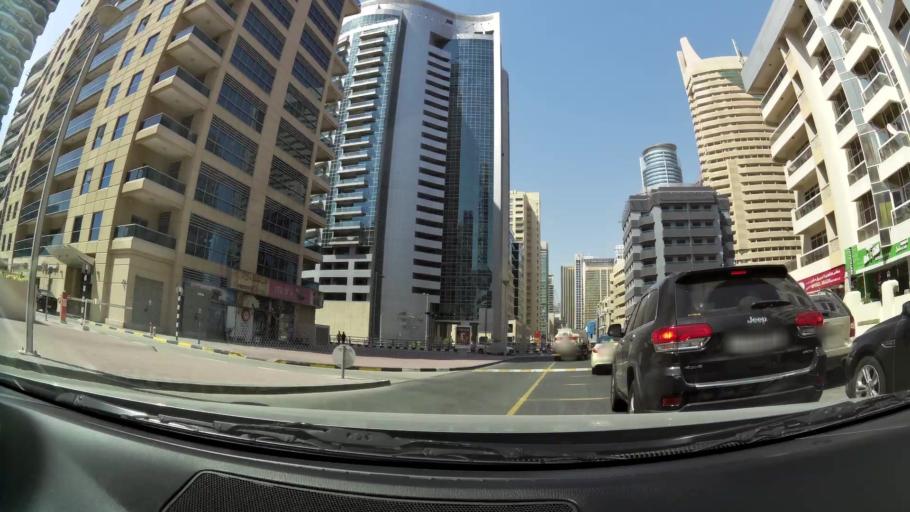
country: AE
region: Dubai
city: Dubai
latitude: 25.0699
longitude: 55.1340
